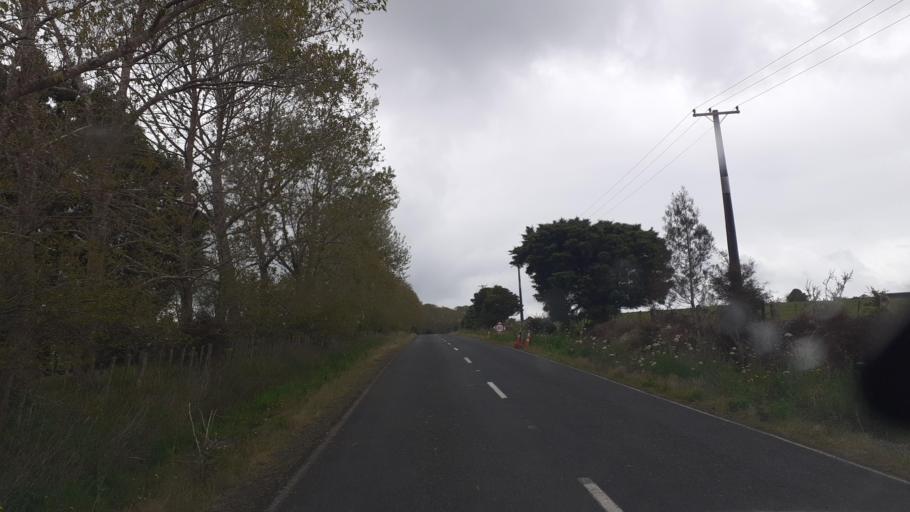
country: NZ
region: Northland
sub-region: Far North District
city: Waimate North
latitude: -35.2713
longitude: 173.8242
